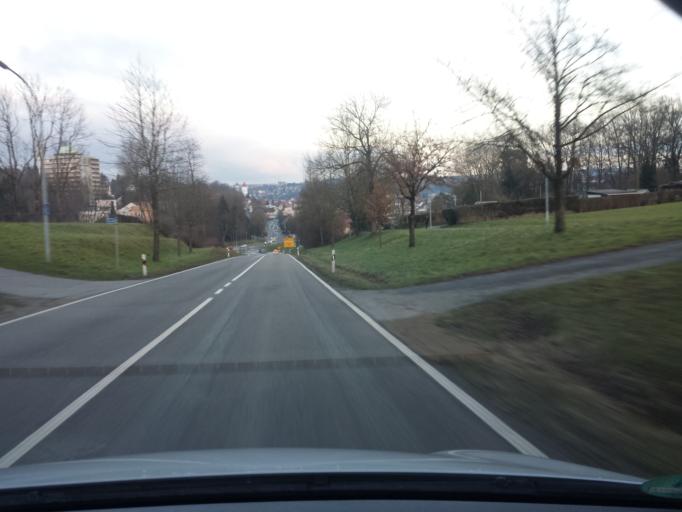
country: DE
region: Baden-Wuerttemberg
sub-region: Tuebingen Region
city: Biberach an der Riss
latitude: 48.0933
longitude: 9.7703
